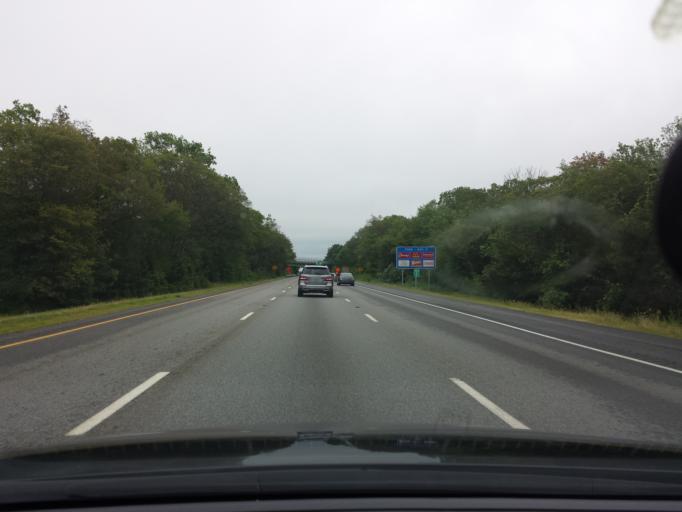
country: US
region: Massachusetts
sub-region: Bristol County
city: Ocean Grove
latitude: 41.7573
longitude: -71.2268
